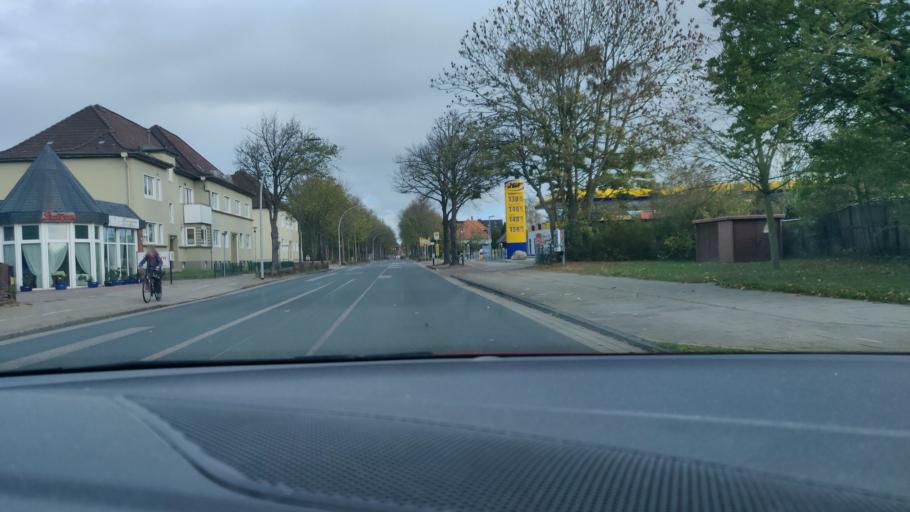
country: DE
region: Lower Saxony
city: Cuxhaven
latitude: 53.8596
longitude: 8.6819
